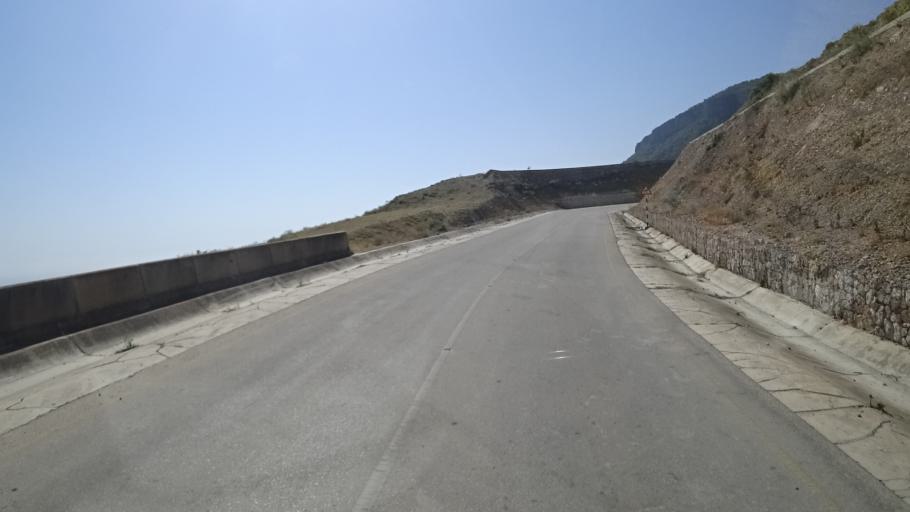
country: OM
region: Zufar
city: Salalah
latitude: 17.0478
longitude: 54.6116
